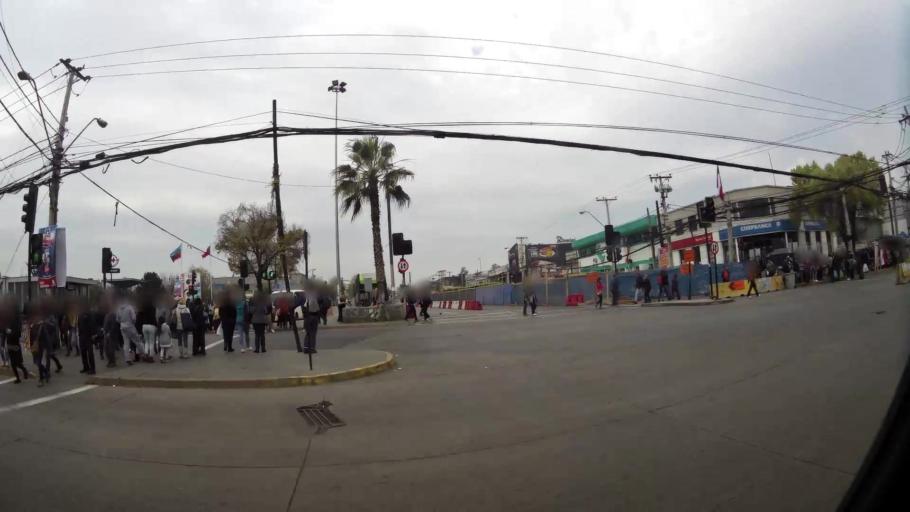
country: CL
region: Santiago Metropolitan
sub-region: Provincia de Santiago
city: Lo Prado
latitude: -33.5106
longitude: -70.7575
